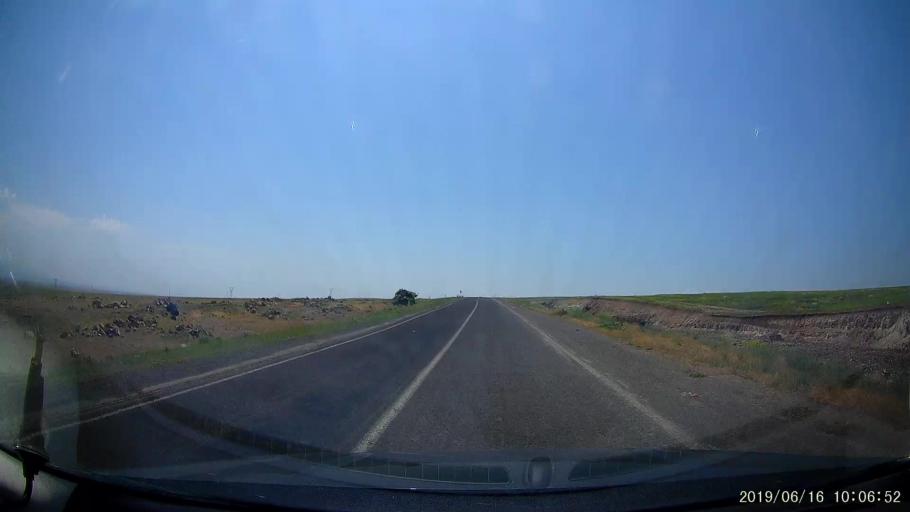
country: TR
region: Kars
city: Digor
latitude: 40.2503
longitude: 43.5480
